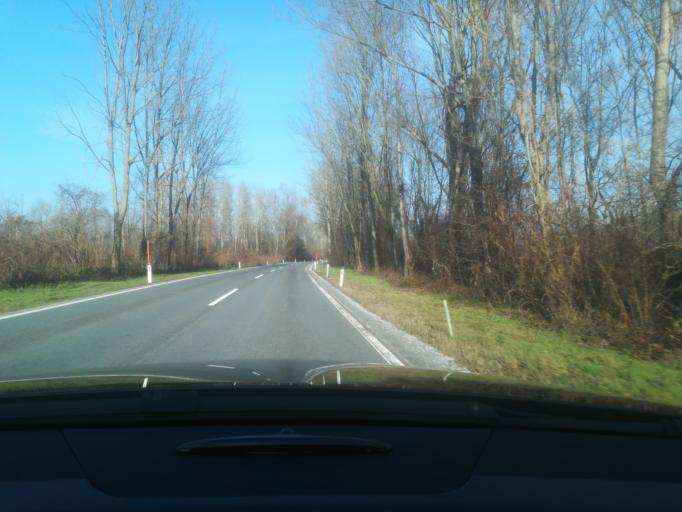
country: AT
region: Upper Austria
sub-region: Politischer Bezirk Urfahr-Umgebung
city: Feldkirchen an der Donau
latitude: 48.3417
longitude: 14.0195
